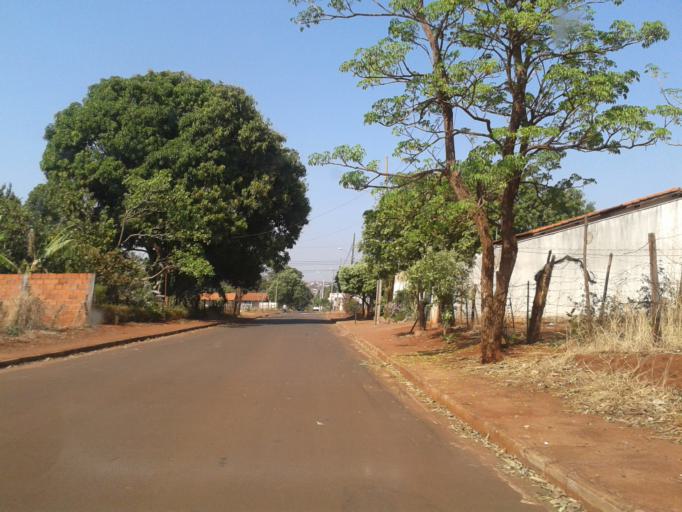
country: BR
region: Minas Gerais
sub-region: Ituiutaba
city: Ituiutaba
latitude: -18.9598
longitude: -49.4817
